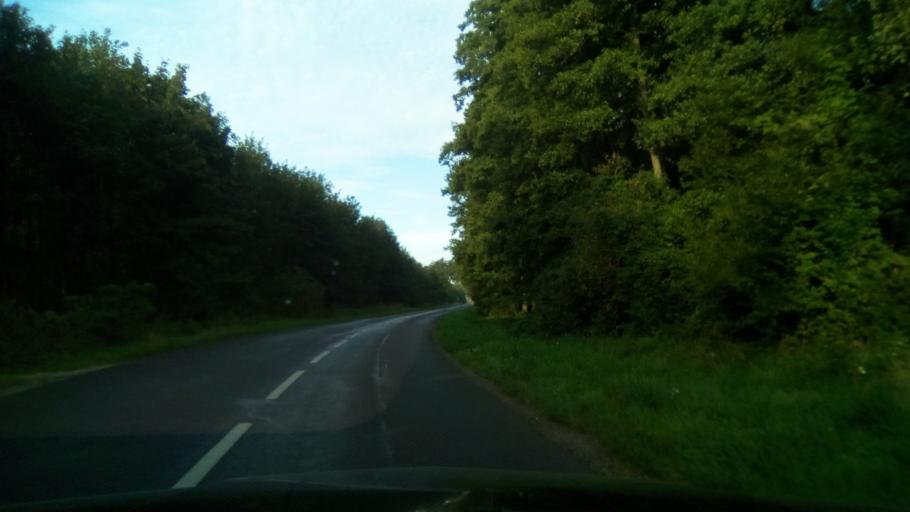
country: PL
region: Greater Poland Voivodeship
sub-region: Powiat chodzieski
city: Margonin
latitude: 52.8758
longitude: 17.1010
